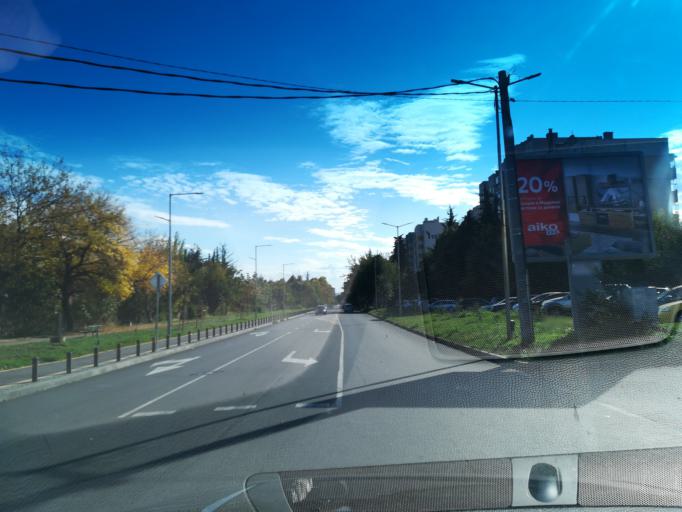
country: BG
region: Stara Zagora
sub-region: Obshtina Stara Zagora
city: Stara Zagora
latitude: 42.4386
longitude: 25.6357
